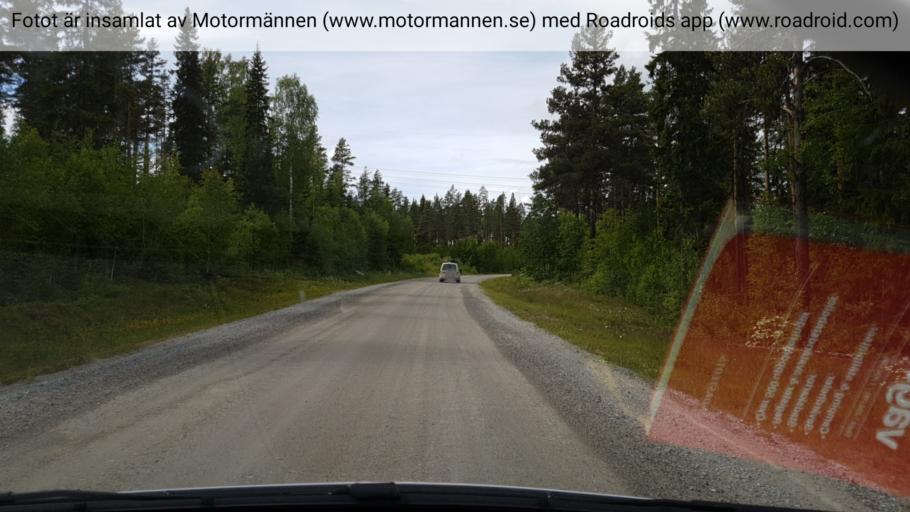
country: SE
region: Vaesternorrland
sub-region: Solleftea Kommun
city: Solleftea
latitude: 63.3137
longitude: 17.2528
